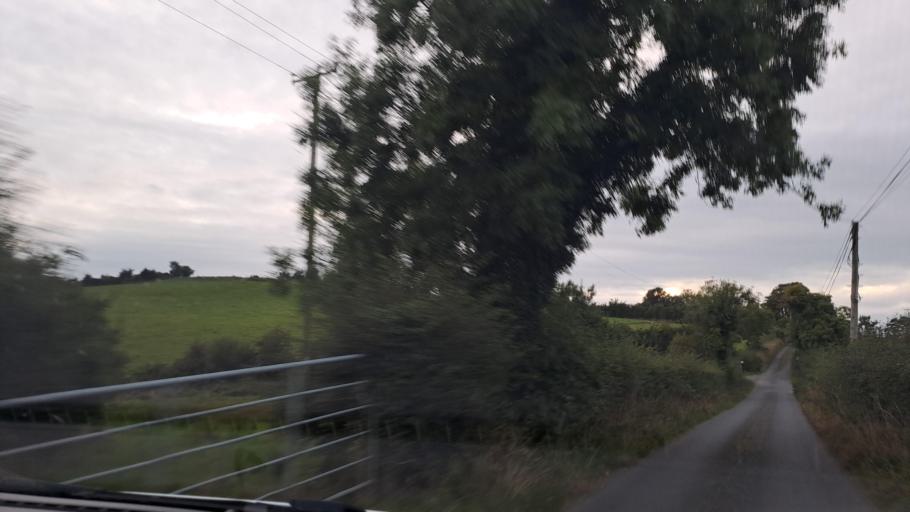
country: IE
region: Ulster
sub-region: An Cabhan
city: Kingscourt
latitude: 53.9886
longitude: -6.8645
